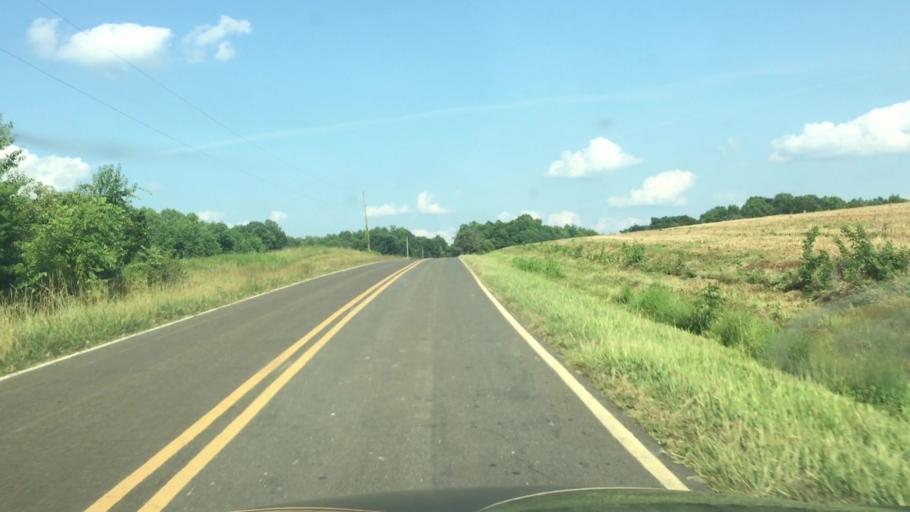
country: US
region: North Carolina
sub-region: Rockingham County
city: Reidsville
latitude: 36.2748
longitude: -79.5758
